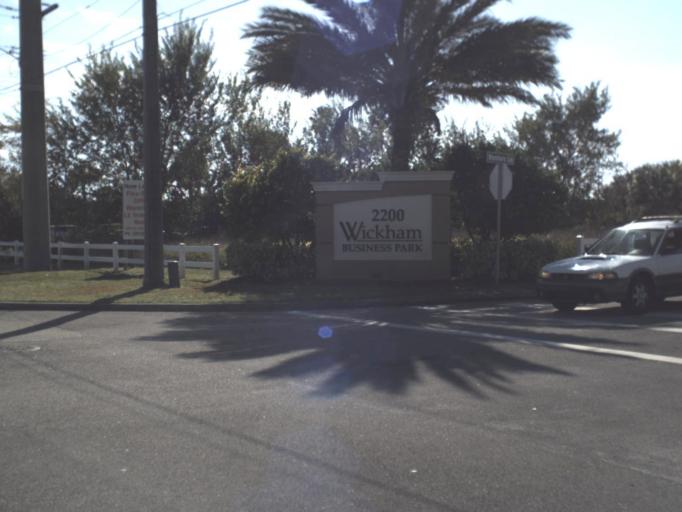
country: US
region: Florida
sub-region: Brevard County
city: June Park
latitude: 28.1423
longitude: -80.6718
